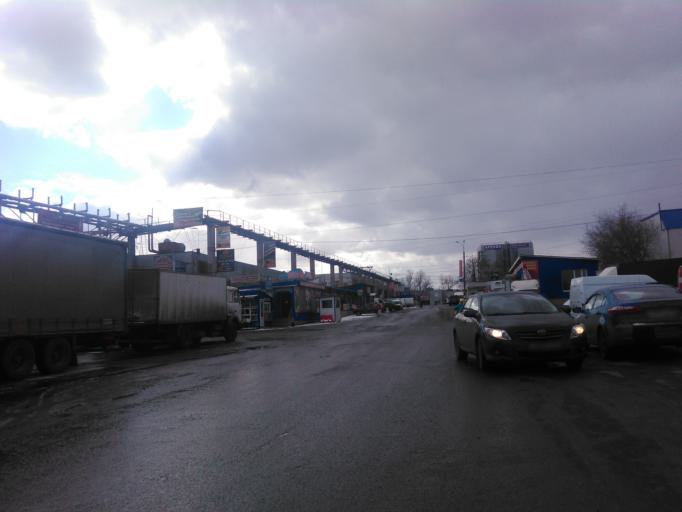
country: RU
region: Moscow
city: Nagornyy
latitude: 55.6499
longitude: 37.6357
